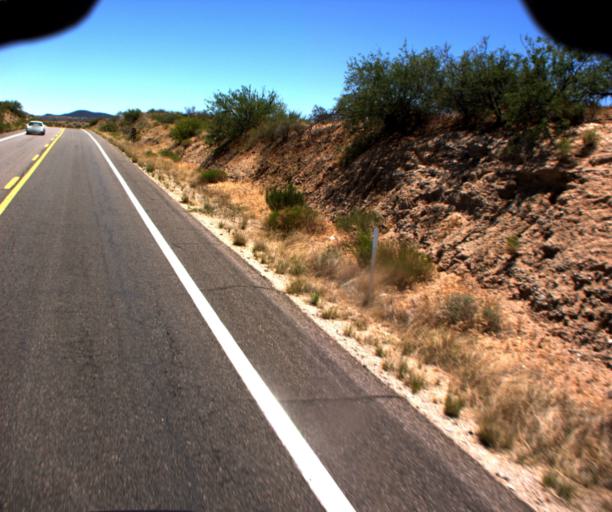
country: US
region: Arizona
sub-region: Gila County
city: Globe
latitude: 33.3586
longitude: -110.7356
